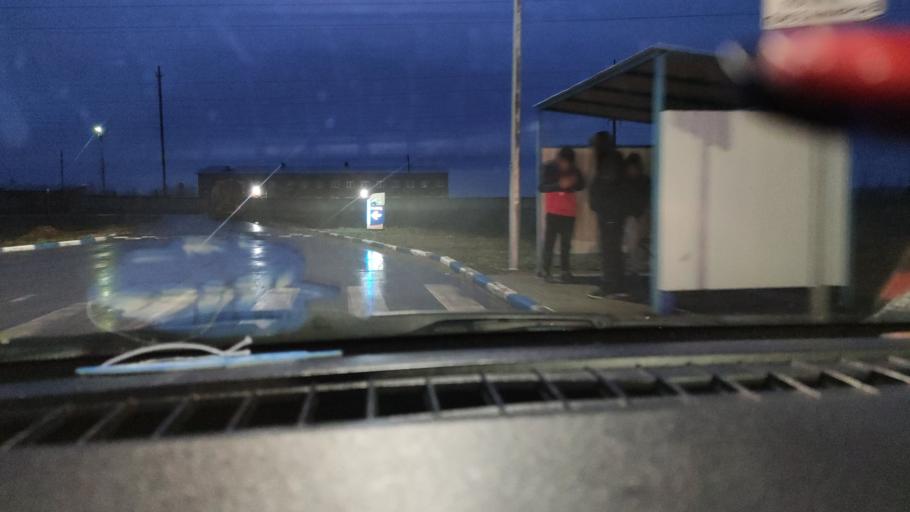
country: RU
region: Udmurtiya
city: Mozhga
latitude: 56.4365
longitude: 52.2506
